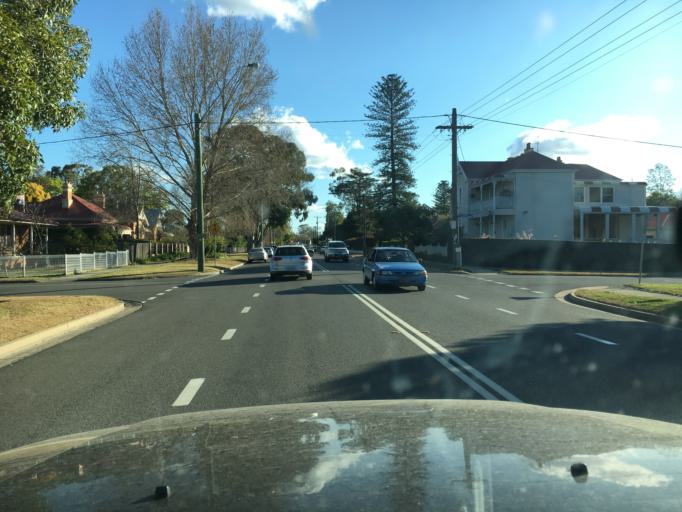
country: AU
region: New South Wales
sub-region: Maitland Municipality
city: Maitland
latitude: -32.7264
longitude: 151.5607
